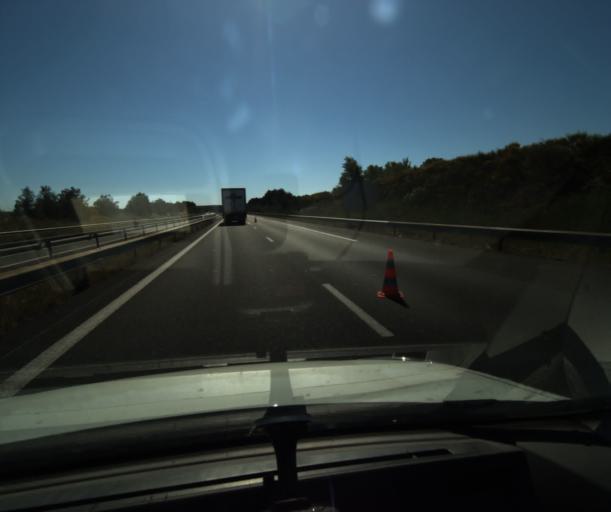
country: FR
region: Languedoc-Roussillon
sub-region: Departement de l'Aude
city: Ferrals-les-Corbieres
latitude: 43.1679
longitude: 2.7164
